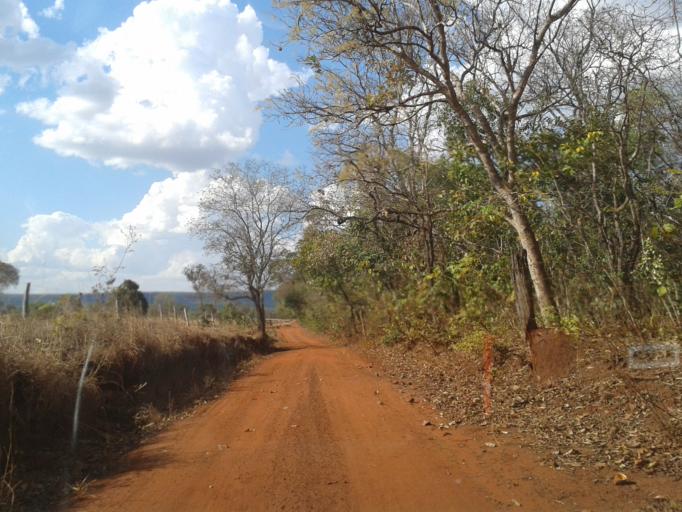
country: BR
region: Minas Gerais
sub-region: Santa Vitoria
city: Santa Vitoria
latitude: -19.1828
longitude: -50.0277
